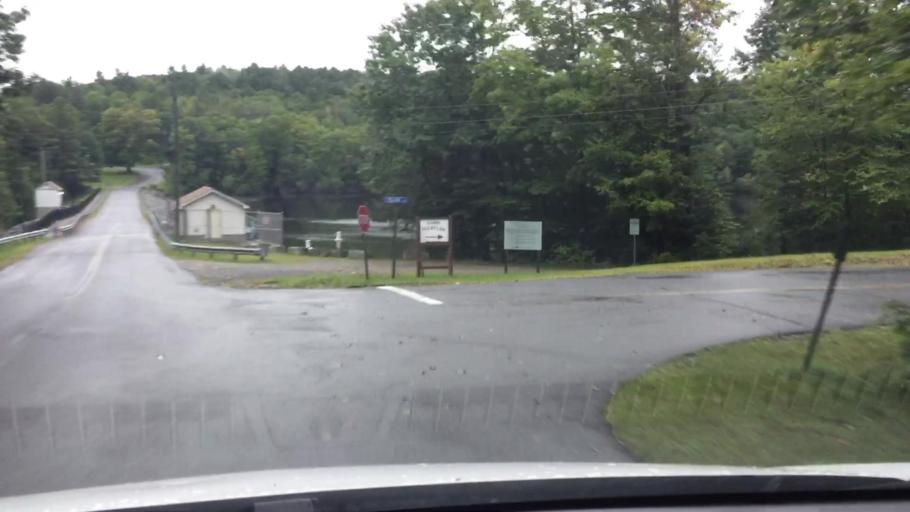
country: US
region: Massachusetts
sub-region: Berkshire County
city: Otis
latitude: 42.1582
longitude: -73.0593
